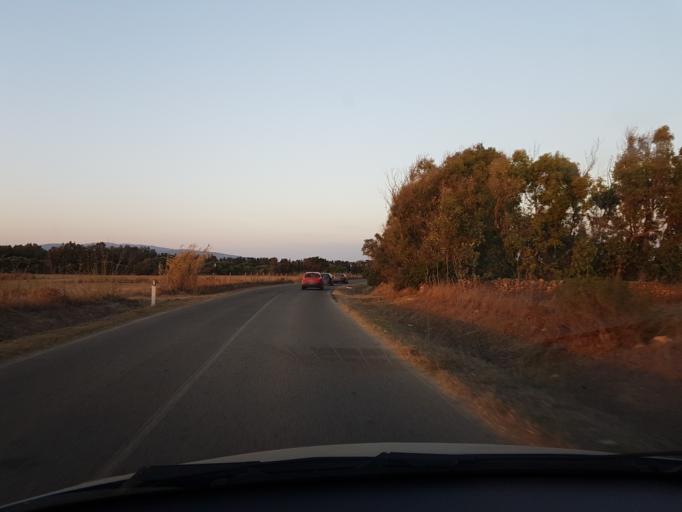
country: IT
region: Sardinia
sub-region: Provincia di Oristano
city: Riola Sardo
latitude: 39.9919
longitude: 8.4639
